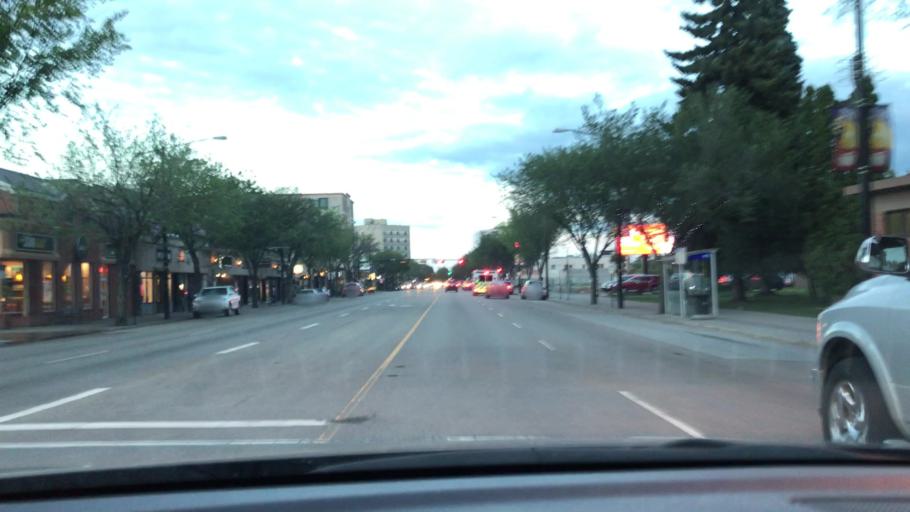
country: CA
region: Alberta
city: Edmonton
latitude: 53.5181
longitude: -113.5063
